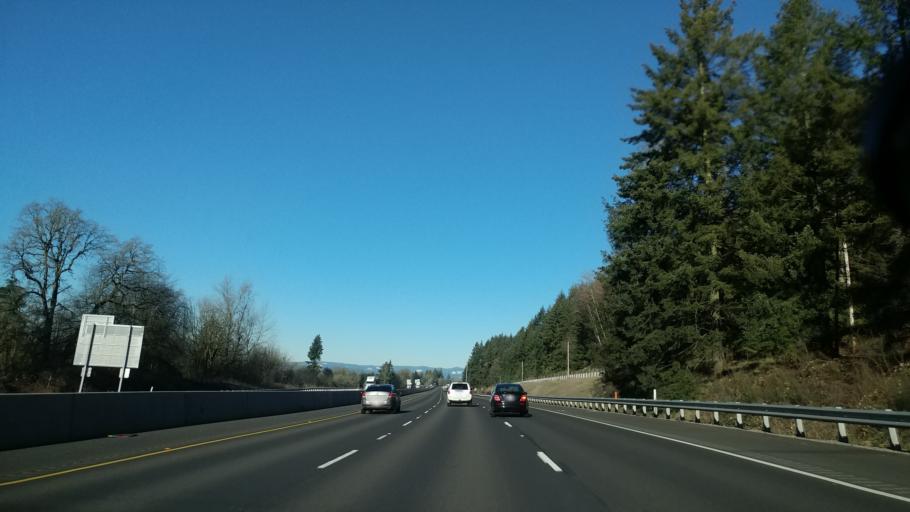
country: US
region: Washington
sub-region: Lewis County
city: Fords Prairie
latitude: 46.7398
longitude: -122.9765
